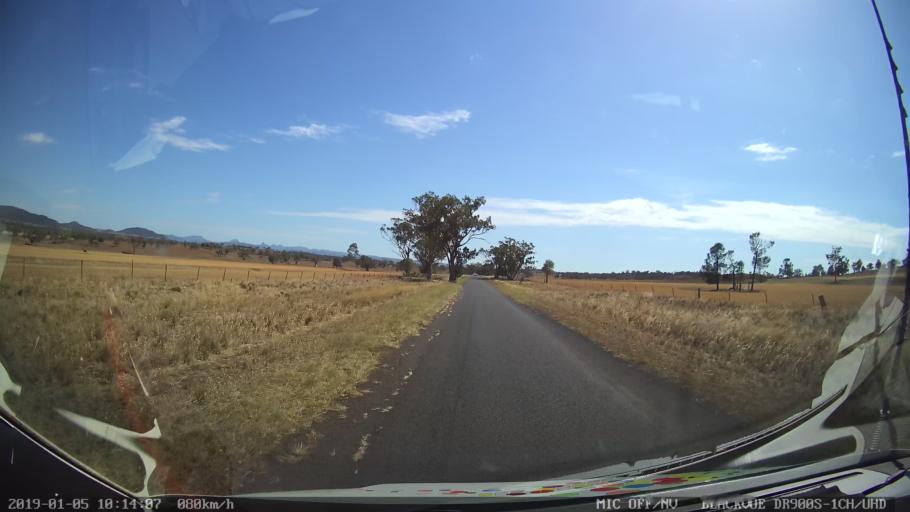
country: AU
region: New South Wales
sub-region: Gilgandra
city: Gilgandra
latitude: -31.5958
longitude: 148.9314
